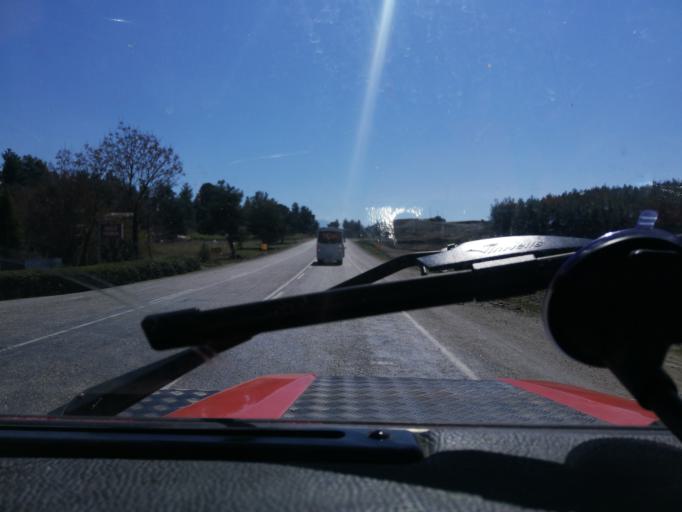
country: TR
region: Mugla
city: Kemer
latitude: 36.6130
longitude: 29.3579
